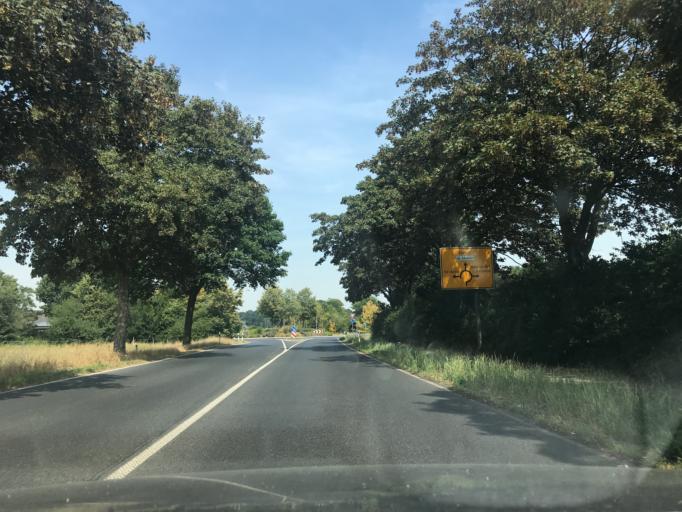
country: DE
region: North Rhine-Westphalia
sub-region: Regierungsbezirk Dusseldorf
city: Issum
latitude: 51.4935
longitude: 6.4173
